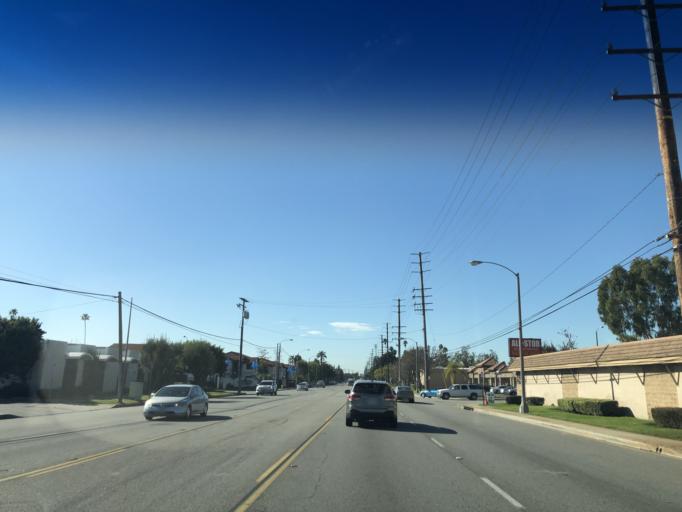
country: US
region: California
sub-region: Los Angeles County
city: Santa Fe Springs
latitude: 33.9354
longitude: -118.0751
